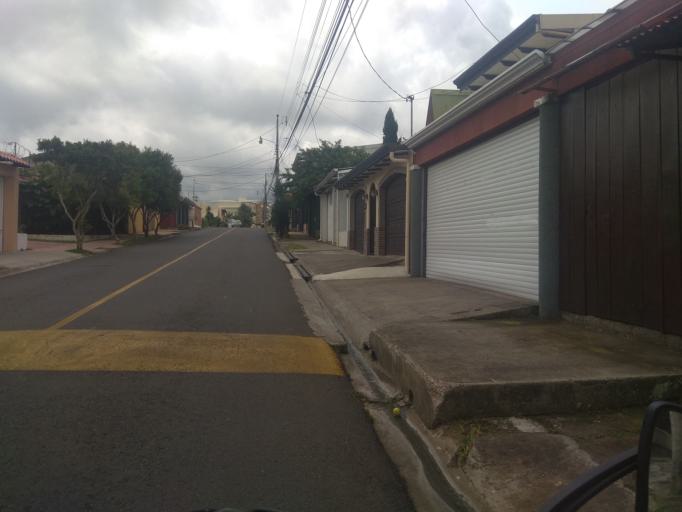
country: CR
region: Heredia
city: San Pablo
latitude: 10.0017
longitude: -84.1005
